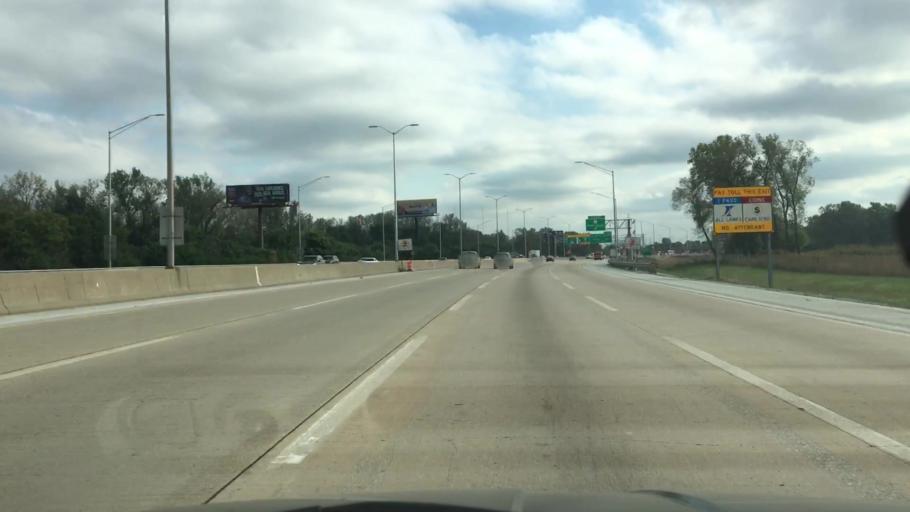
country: US
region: Illinois
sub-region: Cook County
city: University Park
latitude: 41.6097
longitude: -87.6825
